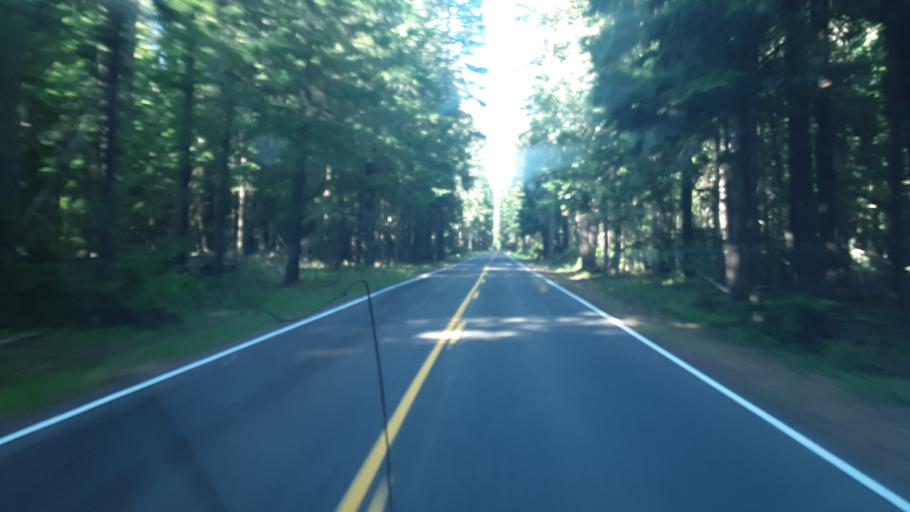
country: US
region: Oregon
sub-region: Jackson County
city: Shady Cove
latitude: 42.9471
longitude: -122.4122
